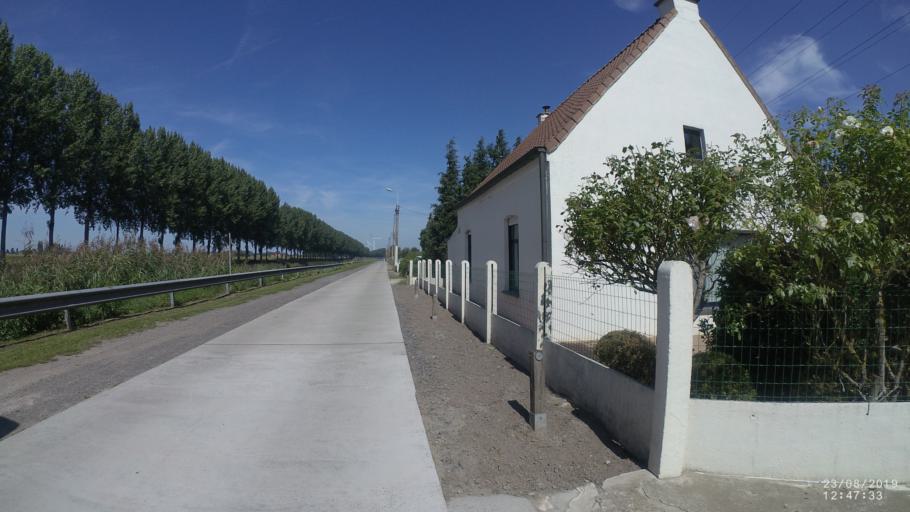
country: BE
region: Flanders
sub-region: Provincie Oost-Vlaanderen
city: Eeklo
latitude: 51.1632
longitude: 3.5449
